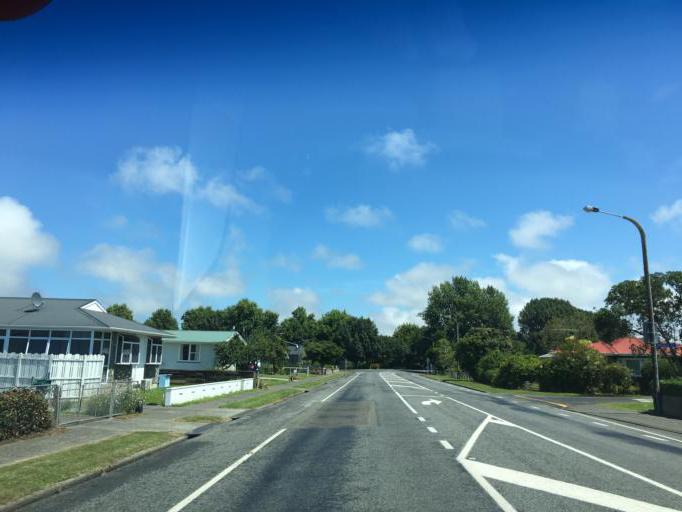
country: NZ
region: Hawke's Bay
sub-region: Wairoa District
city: Wairoa
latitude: -39.0370
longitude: 177.4157
